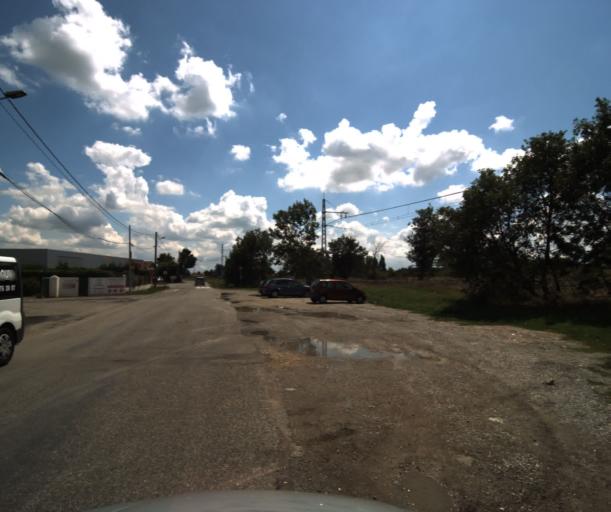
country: FR
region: Midi-Pyrenees
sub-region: Departement de la Haute-Garonne
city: Lacroix-Falgarde
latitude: 43.4923
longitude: 1.3939
